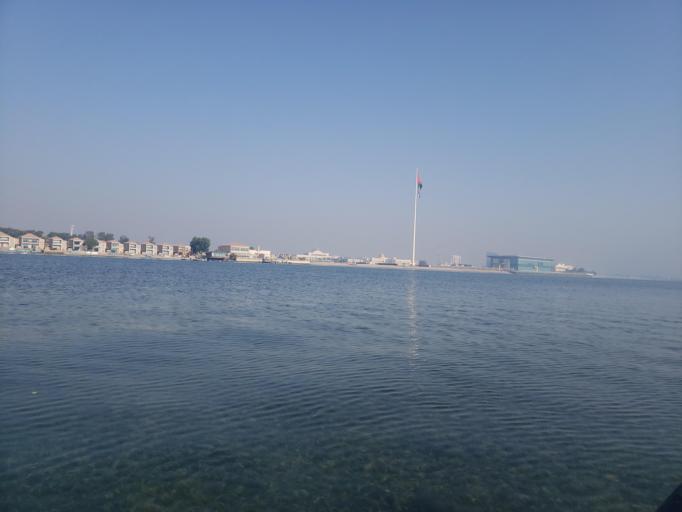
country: AE
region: Umm al Qaywayn
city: Umm al Qaywayn
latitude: 25.5635
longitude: 55.5693
